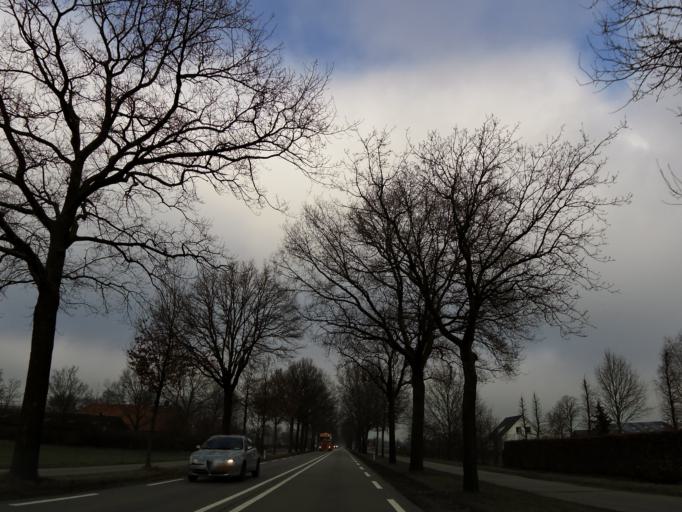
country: NL
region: North Brabant
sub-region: Gemeente Mill en Sint Hubert
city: Wilbertoord
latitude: 51.5864
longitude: 5.7633
